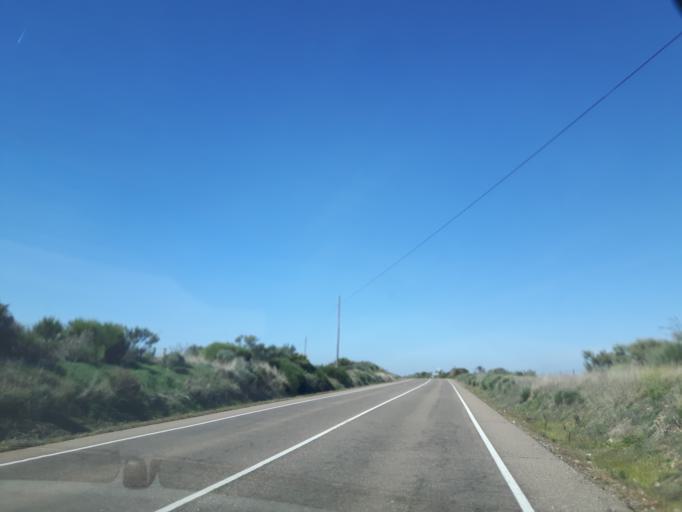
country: ES
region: Castille and Leon
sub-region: Provincia de Salamanca
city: Cerralbo
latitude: 40.9714
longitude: -6.6038
